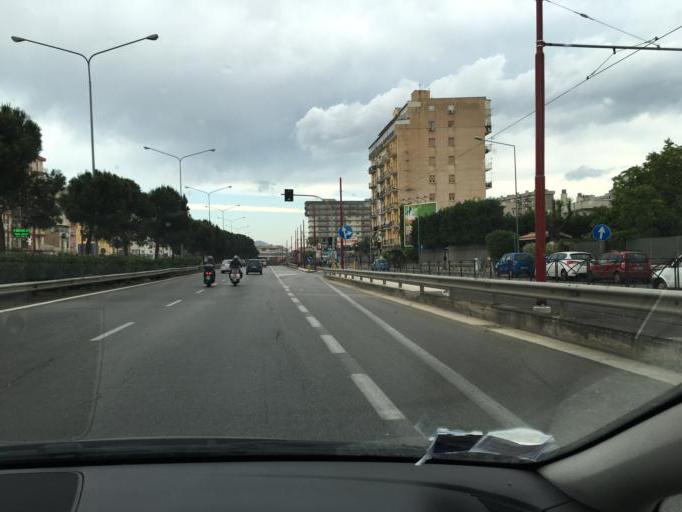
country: IT
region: Sicily
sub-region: Palermo
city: Palermo
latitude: 38.1121
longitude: 13.3297
